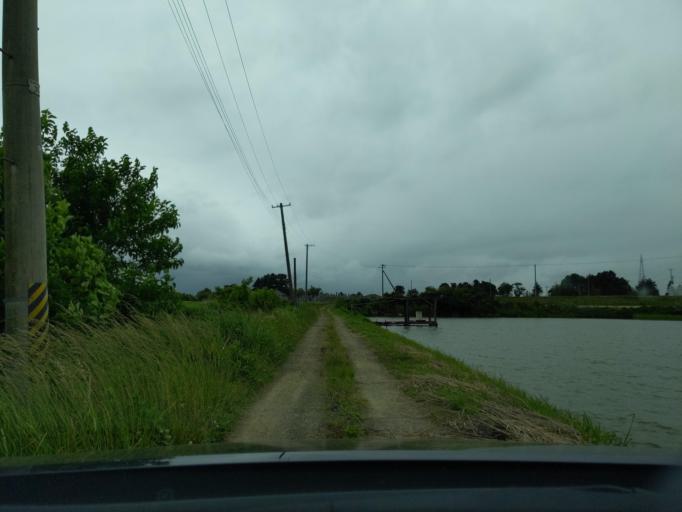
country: JP
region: Fukushima
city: Koriyama
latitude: 37.3686
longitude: 140.3171
